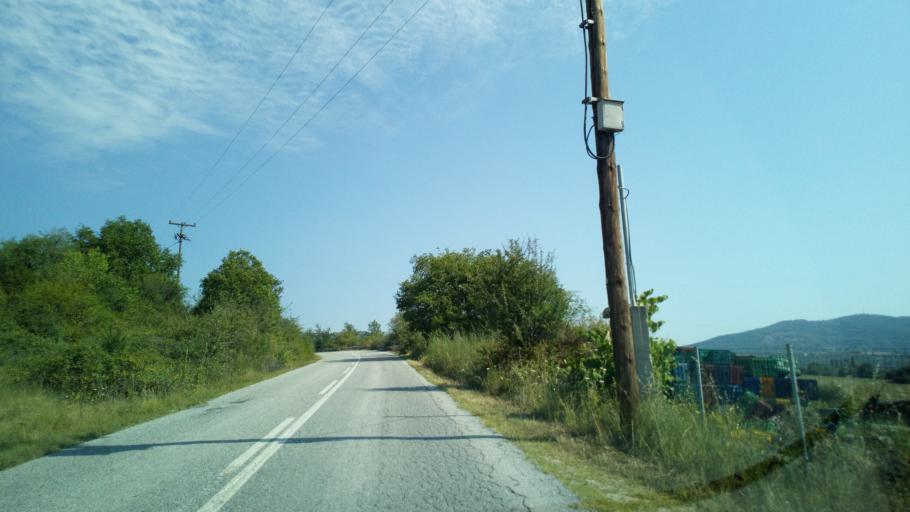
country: GR
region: Central Macedonia
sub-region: Nomos Thessalonikis
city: Askos
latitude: 40.7868
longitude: 23.3764
